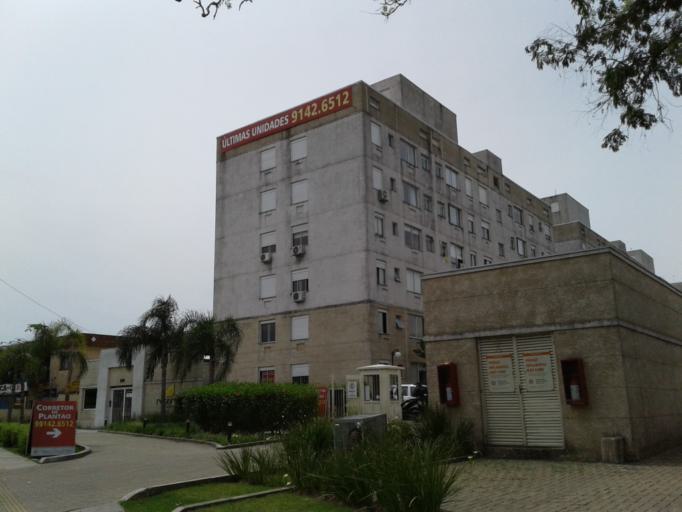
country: BR
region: Rio Grande do Sul
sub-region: Porto Alegre
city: Porto Alegre
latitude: -30.1365
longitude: -51.2220
